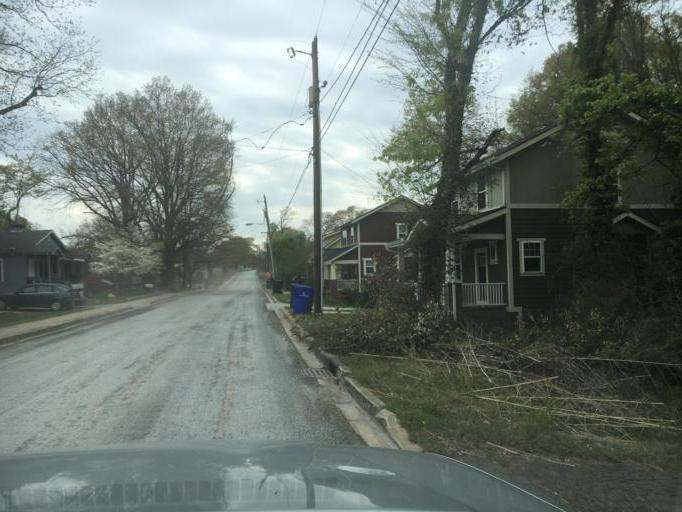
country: US
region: South Carolina
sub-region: Greenville County
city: Greenville
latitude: 34.8617
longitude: -82.3778
